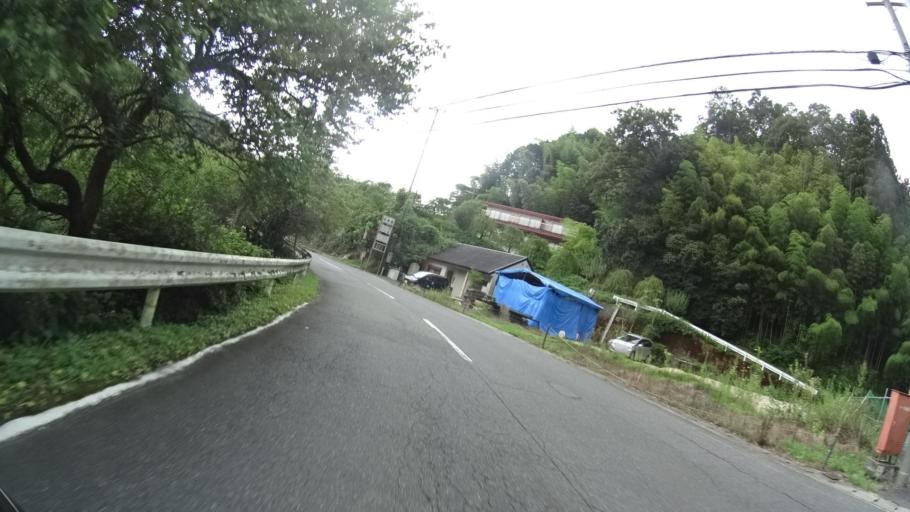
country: JP
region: Mie
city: Nabari
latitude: 34.7076
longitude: 136.0318
